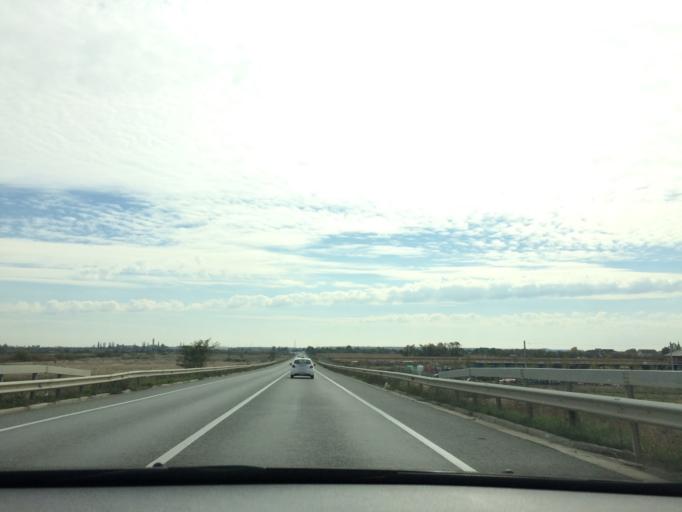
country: RO
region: Timis
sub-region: Comuna Ghiroda
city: Giarmata-Vii
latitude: 45.8071
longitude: 21.2990
